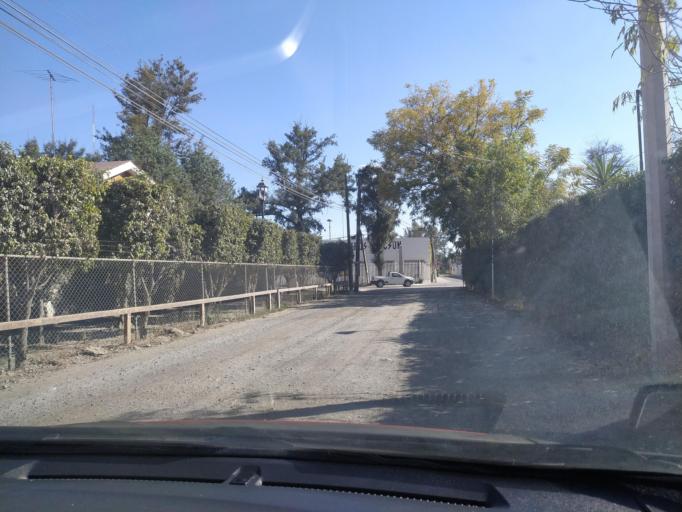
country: LA
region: Oudomxai
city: Muang La
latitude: 21.0254
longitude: 101.8400
